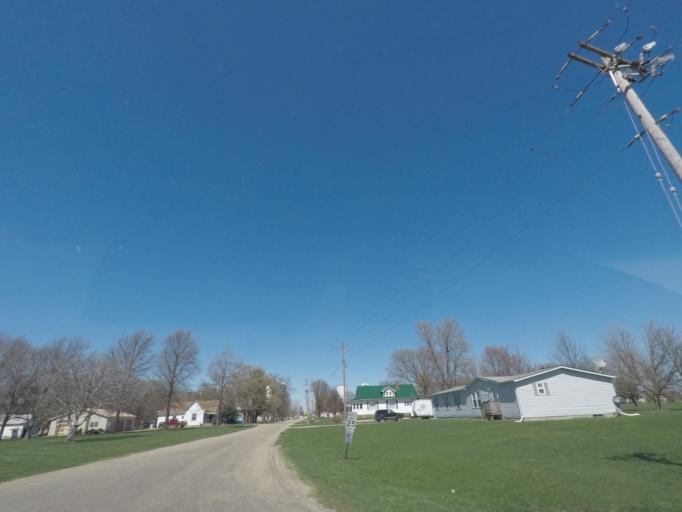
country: US
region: Illinois
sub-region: Macon County
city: Warrensburg
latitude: 39.9613
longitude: -89.1626
